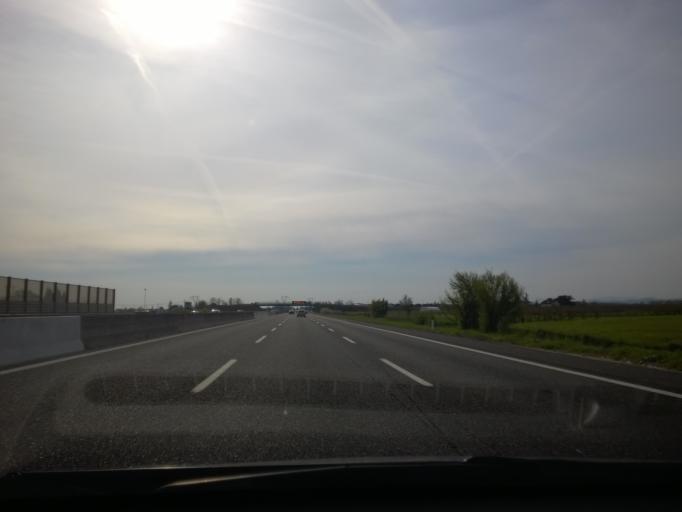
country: IT
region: Emilia-Romagna
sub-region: Forli-Cesena
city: Cesena
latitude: 44.1780
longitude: 12.2659
